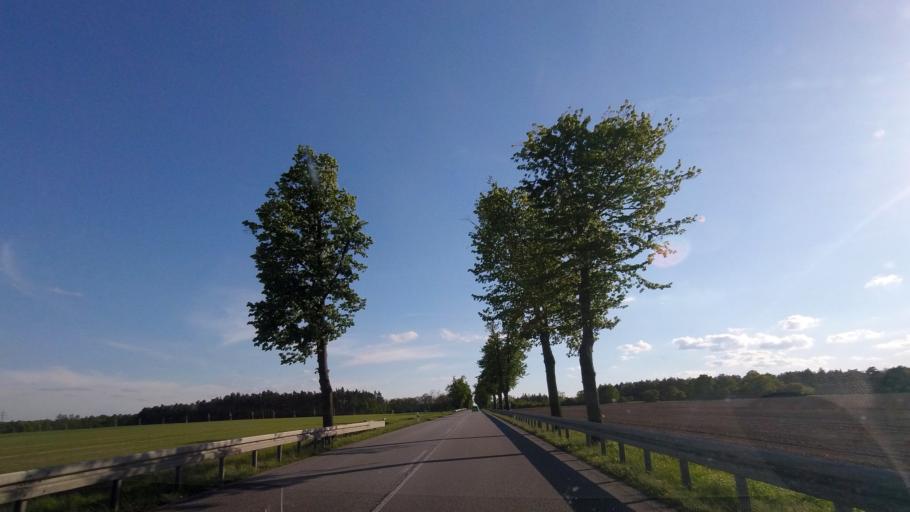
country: DE
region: Brandenburg
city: Luebben
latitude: 51.9232
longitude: 13.8746
